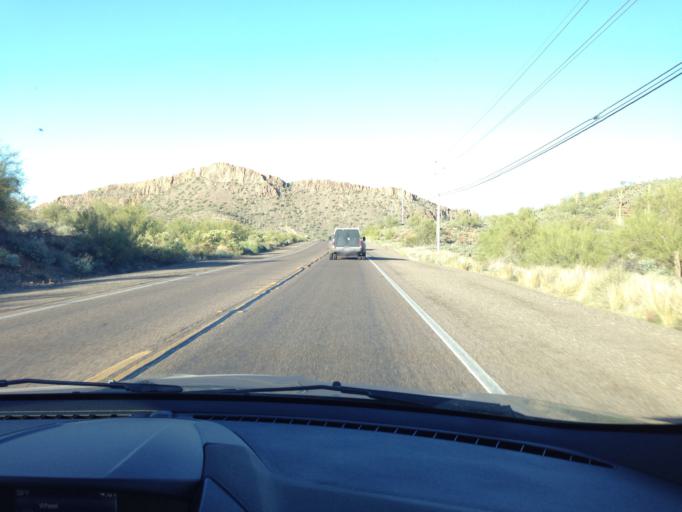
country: US
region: Arizona
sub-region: Maricopa County
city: Anthem
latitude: 33.8591
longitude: -112.0597
